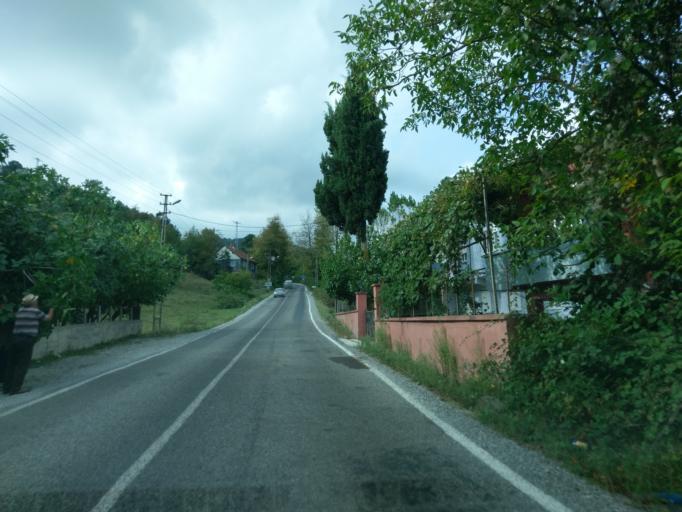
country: TR
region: Sinop
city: Helaldi
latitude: 41.9227
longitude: 34.4142
